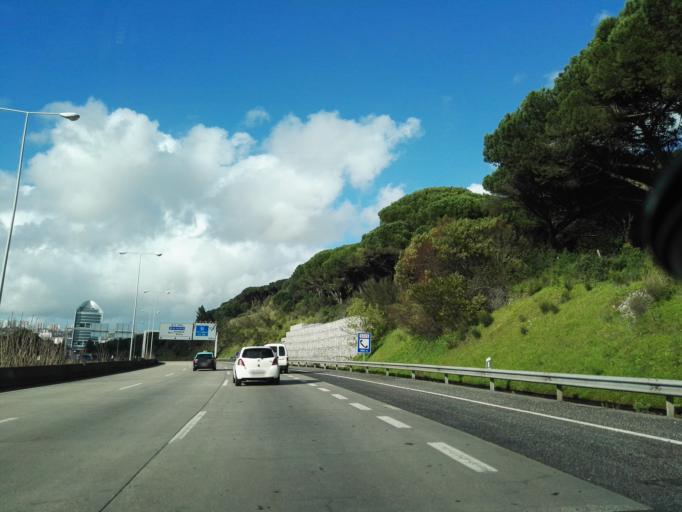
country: PT
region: Lisbon
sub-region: Oeiras
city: Alges
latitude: 38.7076
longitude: -9.2223
